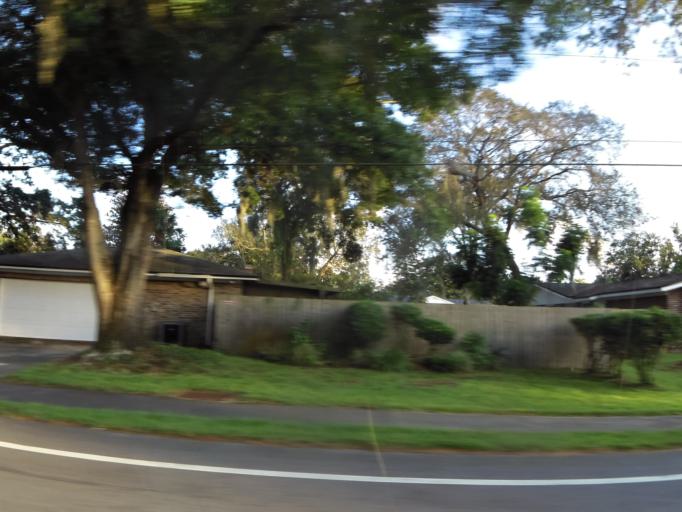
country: US
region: Florida
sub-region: Clay County
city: Orange Park
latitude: 30.2079
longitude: -81.6282
